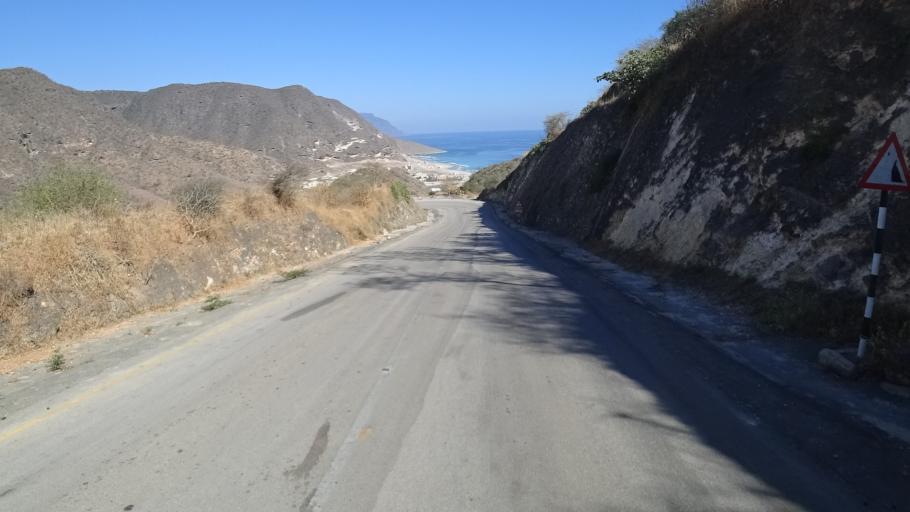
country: YE
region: Al Mahrah
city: Hawf
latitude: 16.7477
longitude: 53.4090
